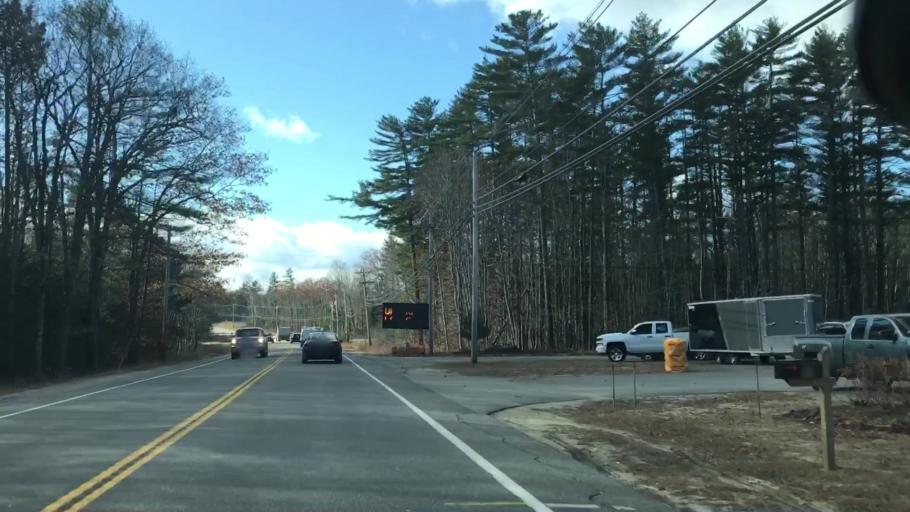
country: US
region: New Hampshire
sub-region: Carroll County
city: Wolfeboro
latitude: 43.6094
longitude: -71.1820
